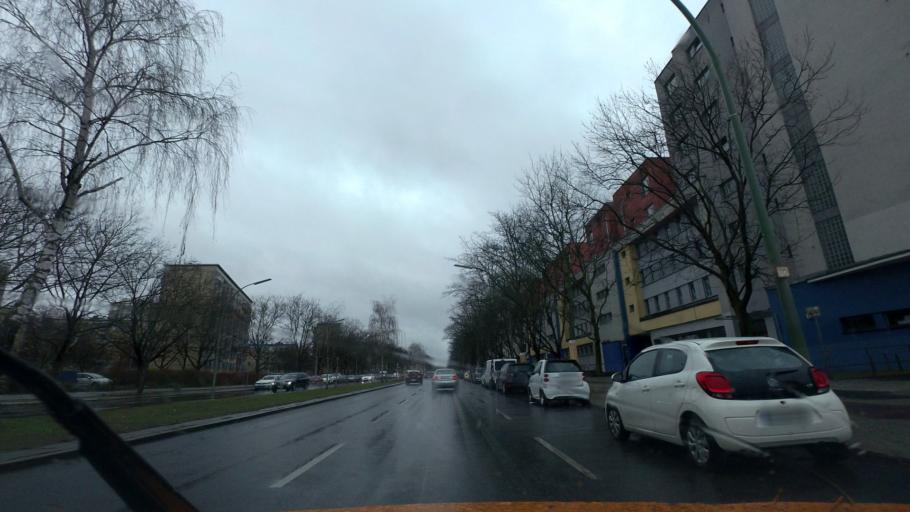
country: DE
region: Berlin
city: Falkenhagener Feld
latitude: 52.5485
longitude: 13.1790
